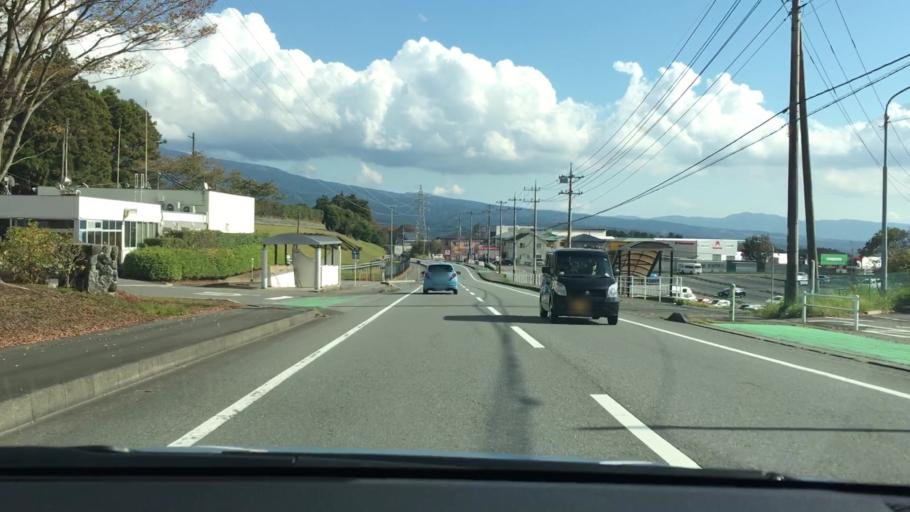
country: JP
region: Shizuoka
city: Gotemba
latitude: 35.2232
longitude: 138.8968
